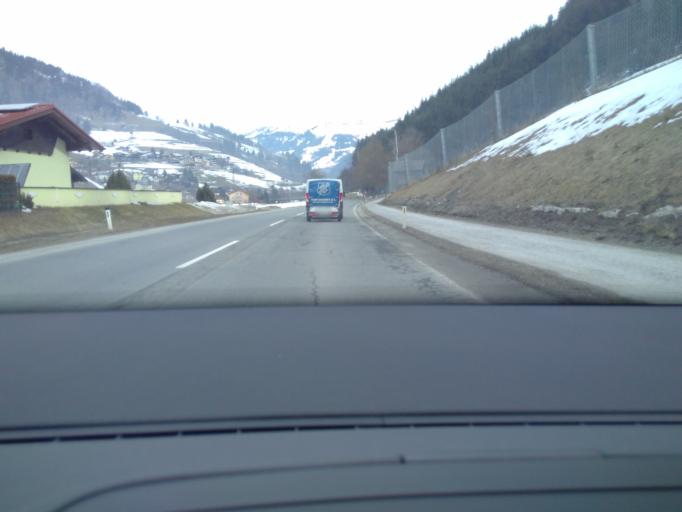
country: AT
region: Salzburg
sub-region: Politischer Bezirk Sankt Johann im Pongau
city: Bad Hofgastein
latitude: 47.1895
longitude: 13.1015
